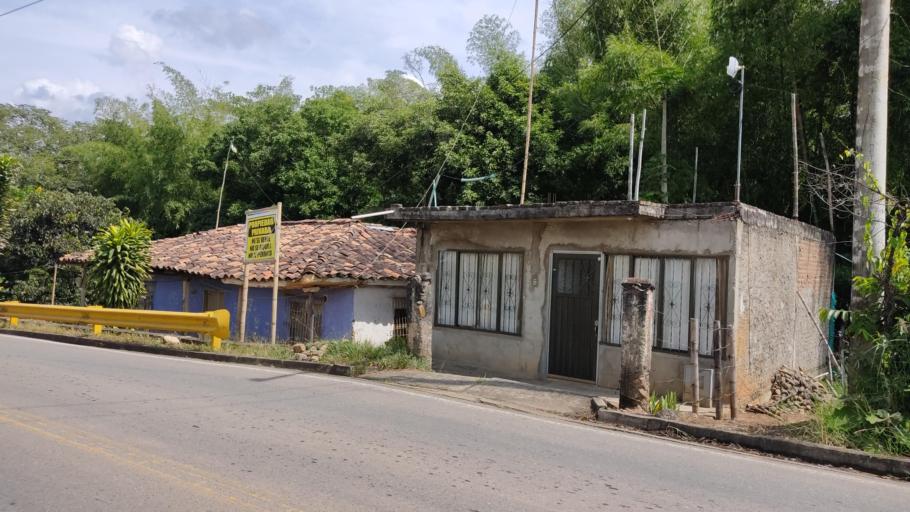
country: CO
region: Cauca
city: Buenos Aires
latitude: 3.1307
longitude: -76.5927
